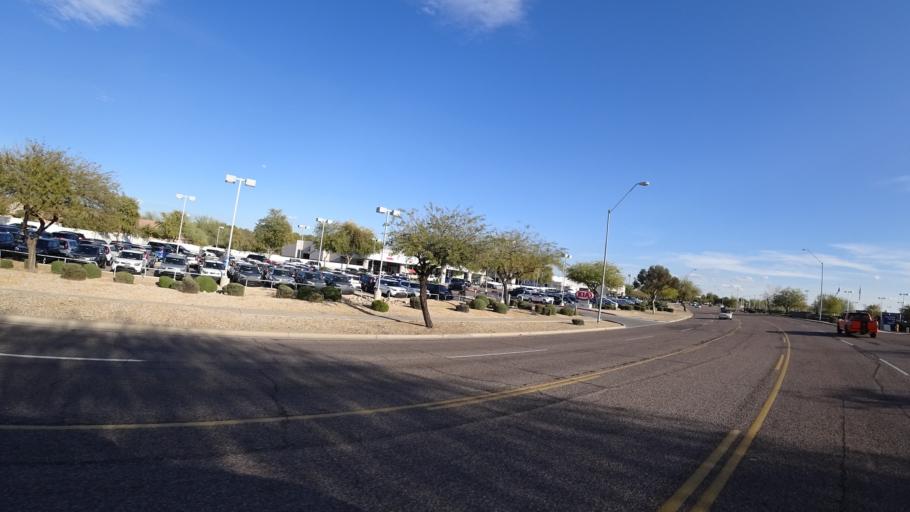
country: US
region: Arizona
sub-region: Maricopa County
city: Sun City
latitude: 33.6421
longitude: -112.2549
